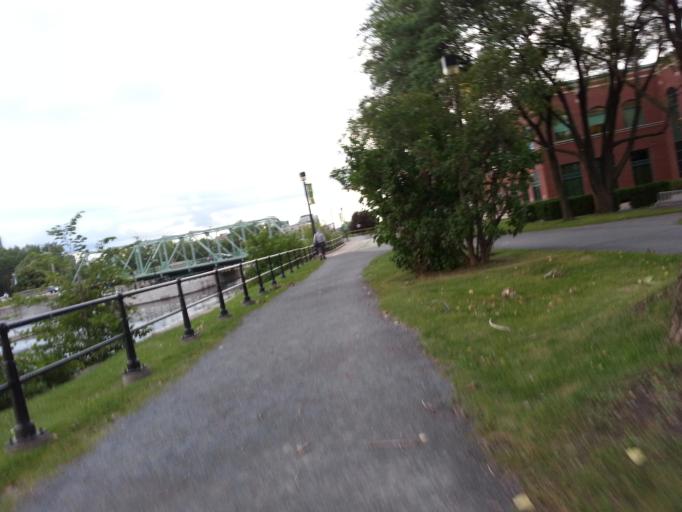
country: CA
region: Quebec
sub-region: Montreal
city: Montreal
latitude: 45.4845
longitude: -73.5667
